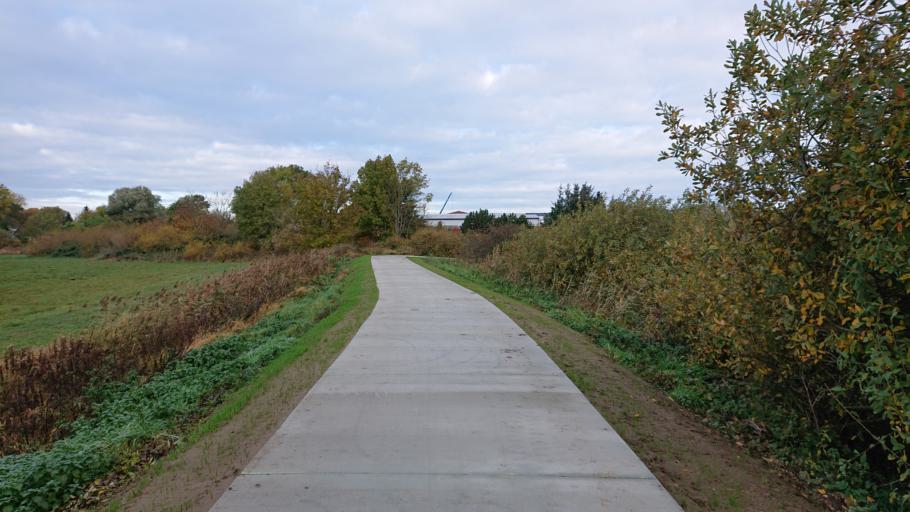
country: DE
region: Mecklenburg-Vorpommern
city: Barth
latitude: 54.3666
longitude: 12.7407
